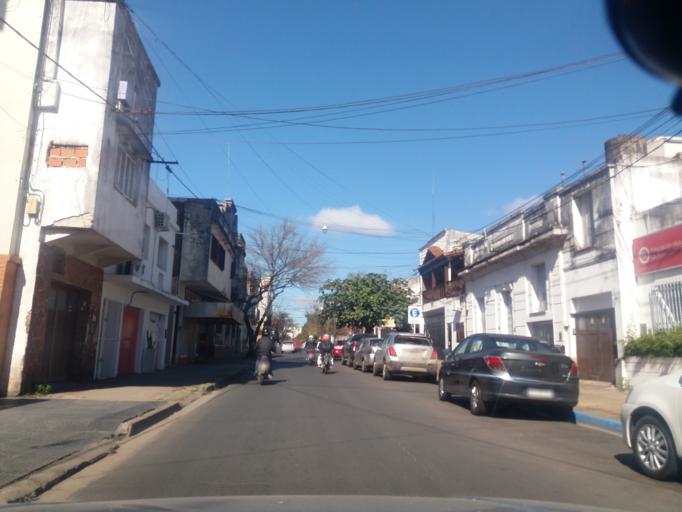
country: AR
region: Corrientes
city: Corrientes
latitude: -27.4726
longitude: -58.8350
